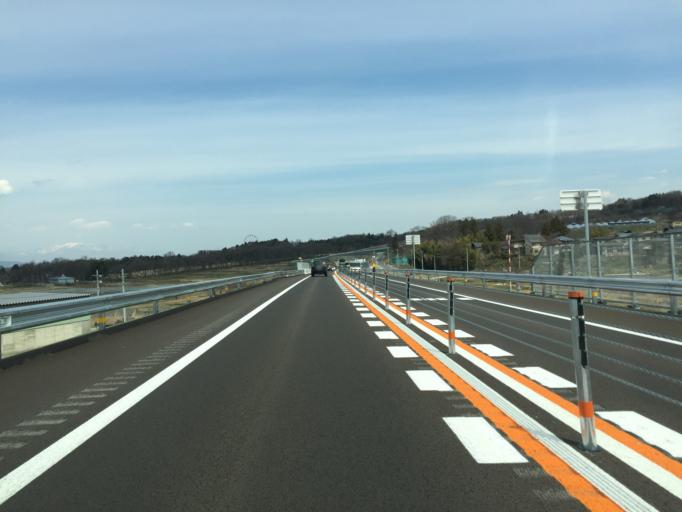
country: JP
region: Yamagata
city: Kaminoyama
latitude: 38.1652
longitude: 140.3086
